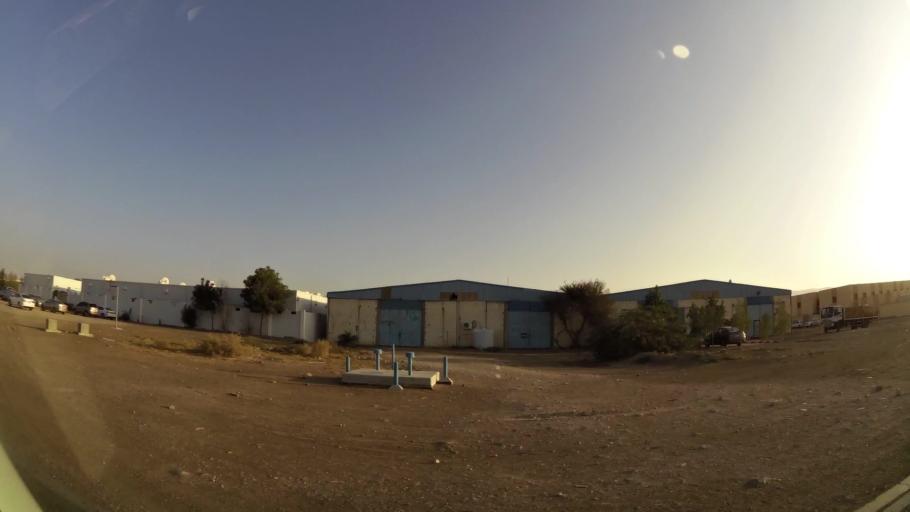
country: AE
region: Abu Dhabi
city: Al Ain
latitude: 24.1516
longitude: 55.8380
